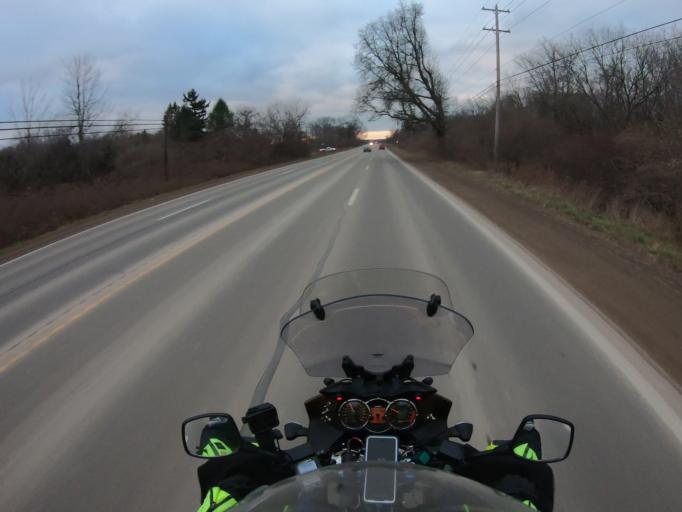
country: US
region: Michigan
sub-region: Genesee County
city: Grand Blanc
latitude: 42.8609
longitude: -83.5807
